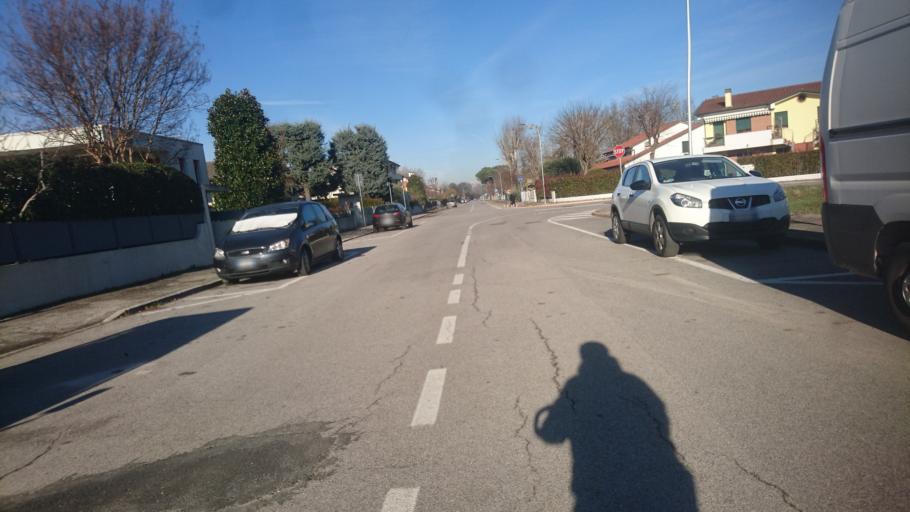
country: IT
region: Veneto
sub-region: Provincia di Padova
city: Limena
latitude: 45.4705
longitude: 11.8423
